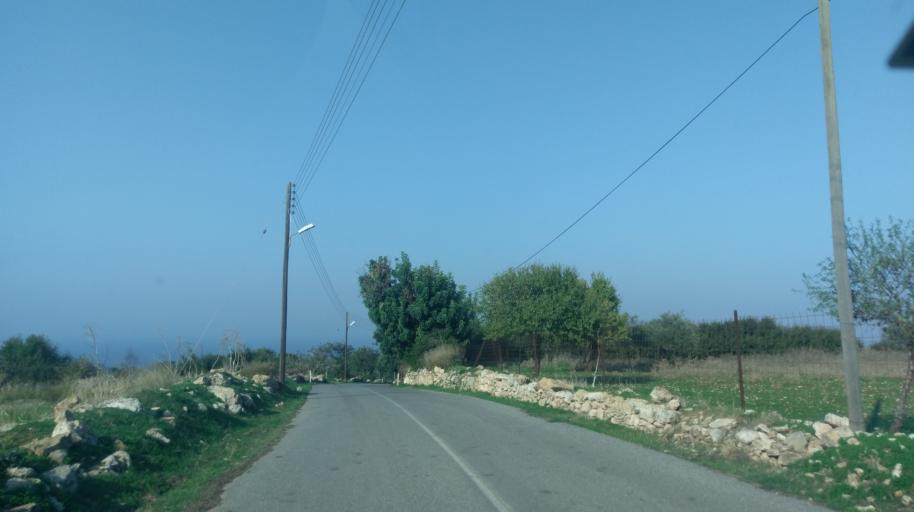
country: CY
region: Ammochostos
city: Leonarisso
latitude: 35.5424
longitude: 34.2235
